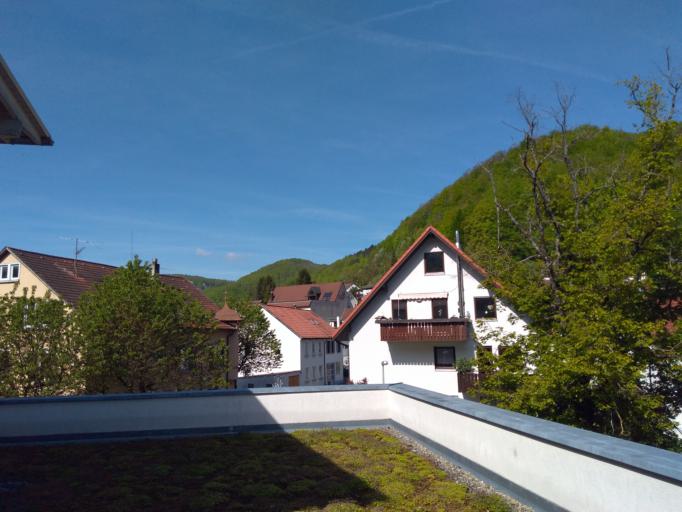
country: DE
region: Baden-Wuerttemberg
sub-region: Tuebingen Region
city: Pfullingen
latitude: 48.4289
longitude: 9.2552
